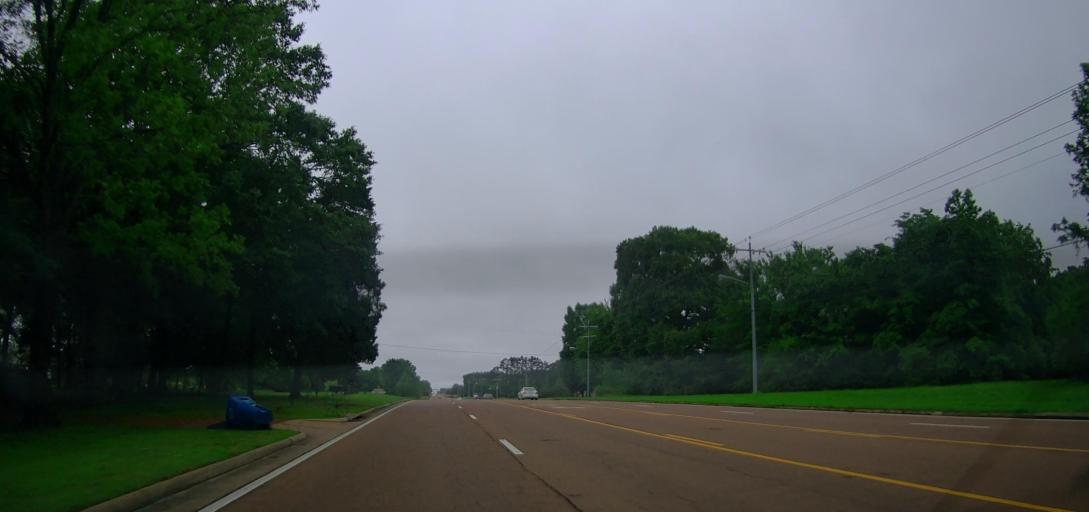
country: US
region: Mississippi
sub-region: De Soto County
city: Olive Branch
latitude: 34.9780
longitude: -89.8307
